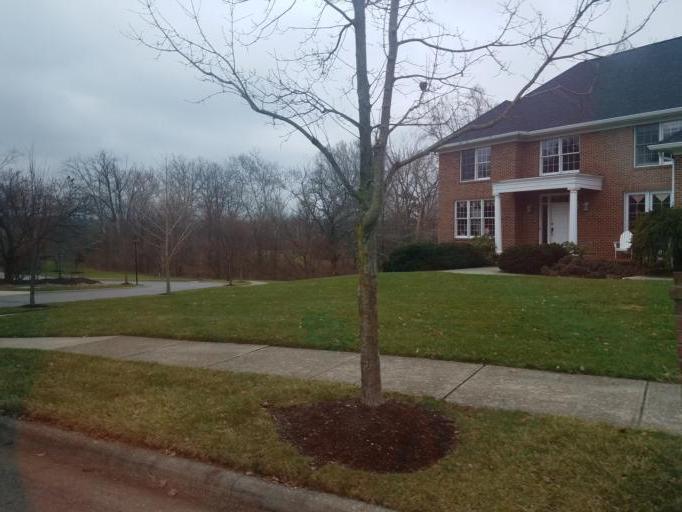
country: US
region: Ohio
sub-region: Franklin County
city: Westerville
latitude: 40.1343
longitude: -82.9533
